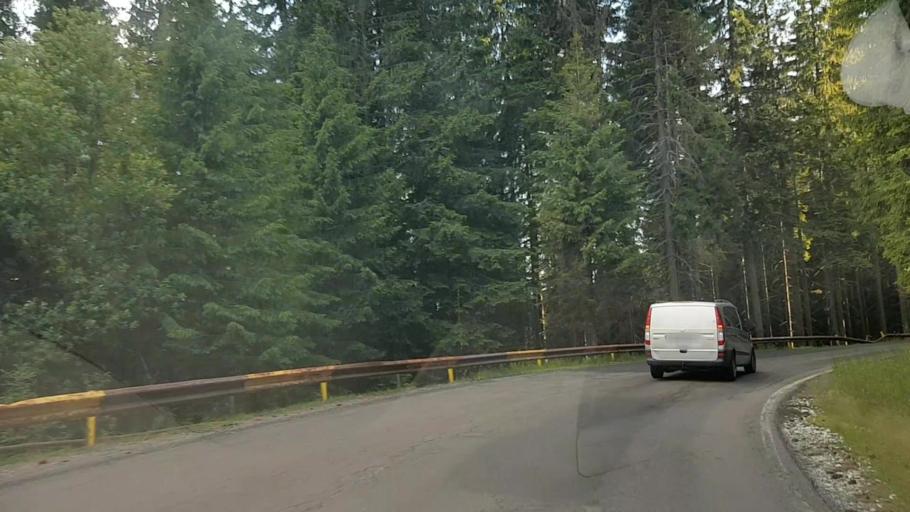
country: RO
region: Harghita
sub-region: Comuna Varsag
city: Varsag
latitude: 46.6618
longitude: 25.3040
